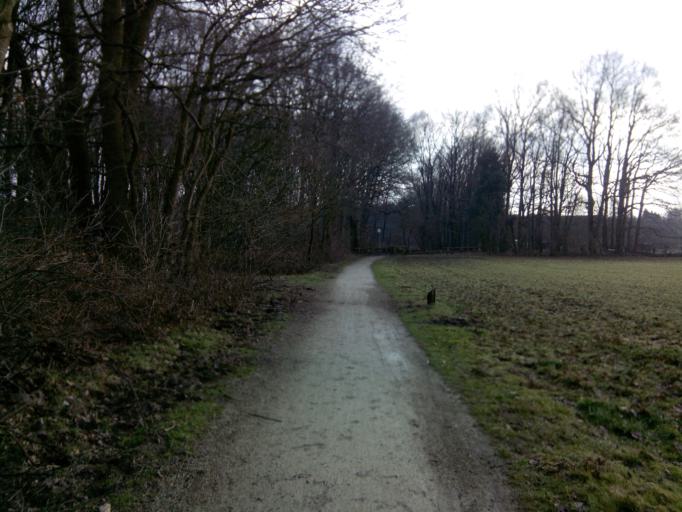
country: NL
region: Utrecht
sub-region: Gemeente Utrechtse Heuvelrug
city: Amerongen
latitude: 52.0011
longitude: 5.4741
